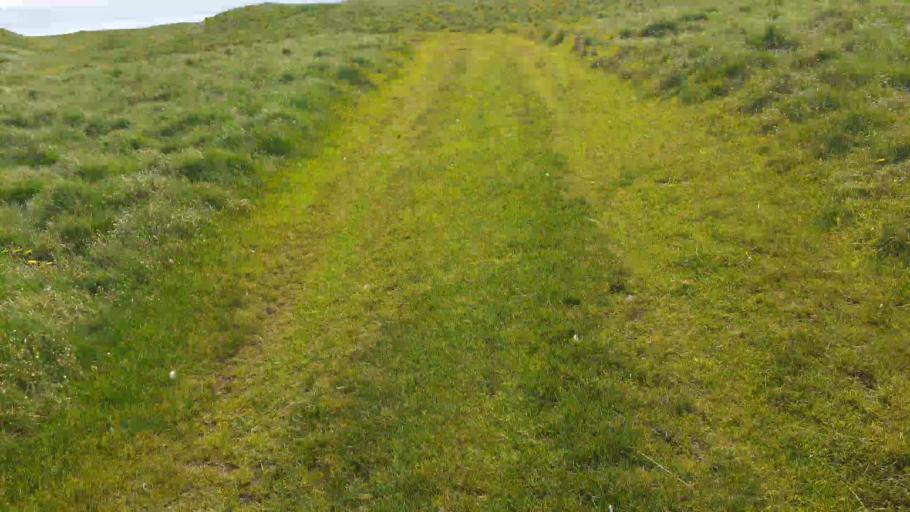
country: IS
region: Northeast
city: Dalvik
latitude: 66.5496
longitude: -17.9924
